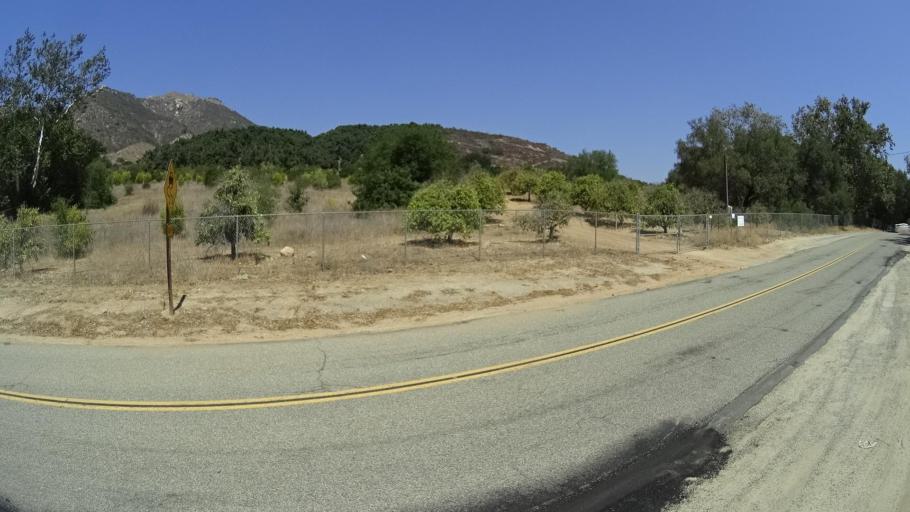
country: US
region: California
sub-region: San Diego County
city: Fallbrook
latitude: 33.4656
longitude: -117.2787
